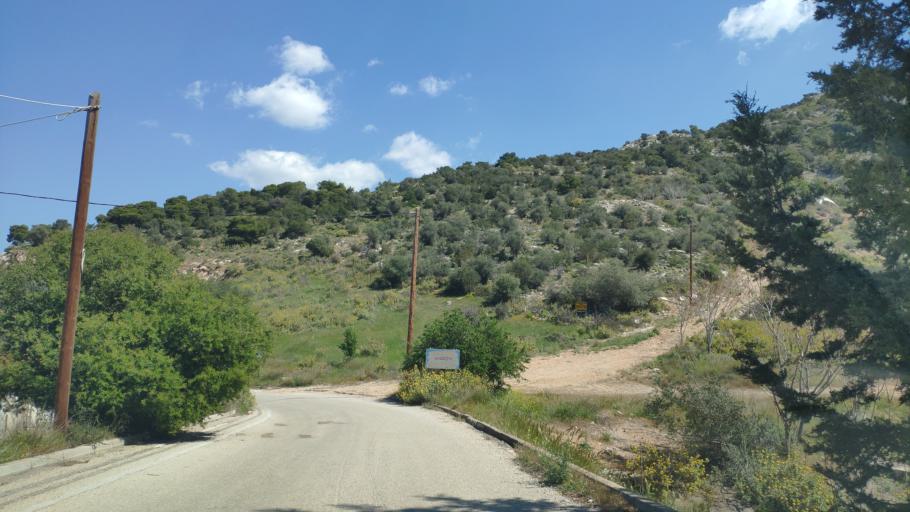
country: GR
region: Attica
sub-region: Nomarchia Athinas
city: Chaidari
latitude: 38.0335
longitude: 23.6373
